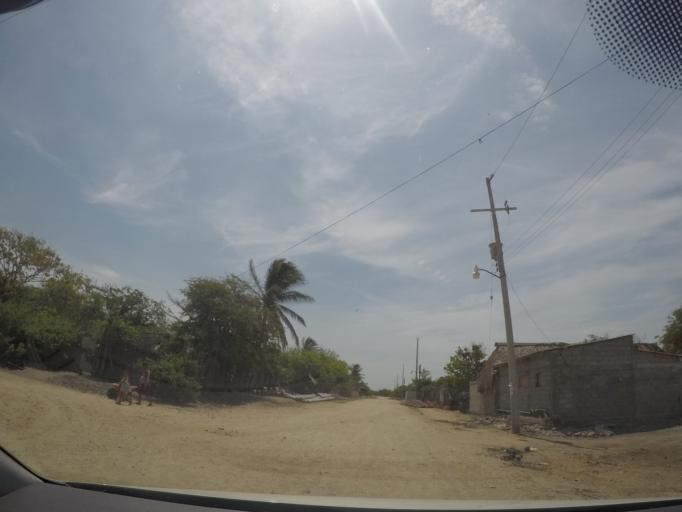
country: MX
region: Oaxaca
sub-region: Salina Cruz
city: Salina Cruz
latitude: 16.1907
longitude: -95.1178
